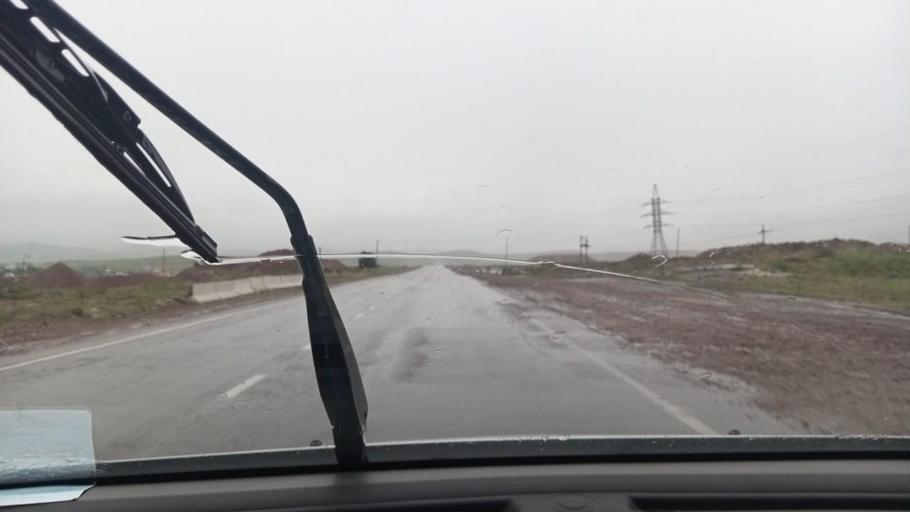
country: UZ
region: Toshkent
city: Angren
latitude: 41.0427
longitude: 70.1541
